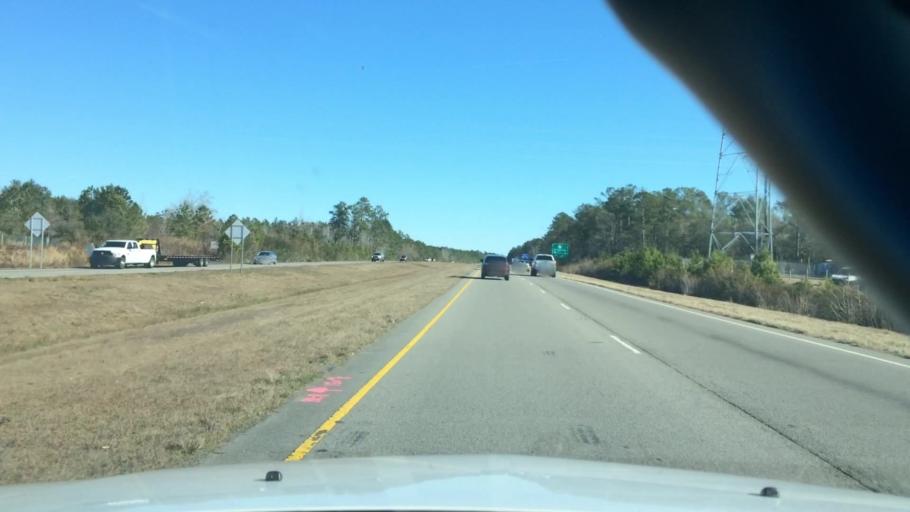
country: US
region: North Carolina
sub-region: Brunswick County
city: Shallotte
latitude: 33.9629
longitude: -78.4162
